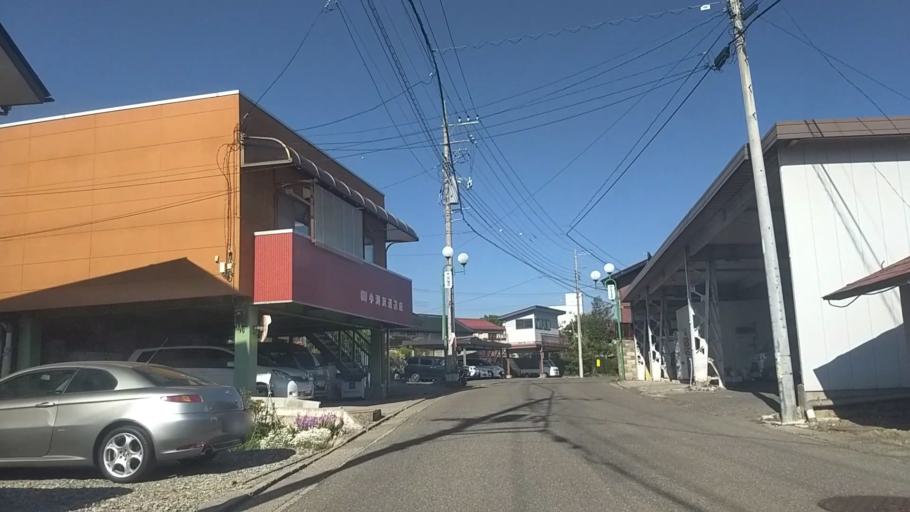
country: JP
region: Nagano
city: Chino
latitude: 35.8624
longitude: 138.3124
